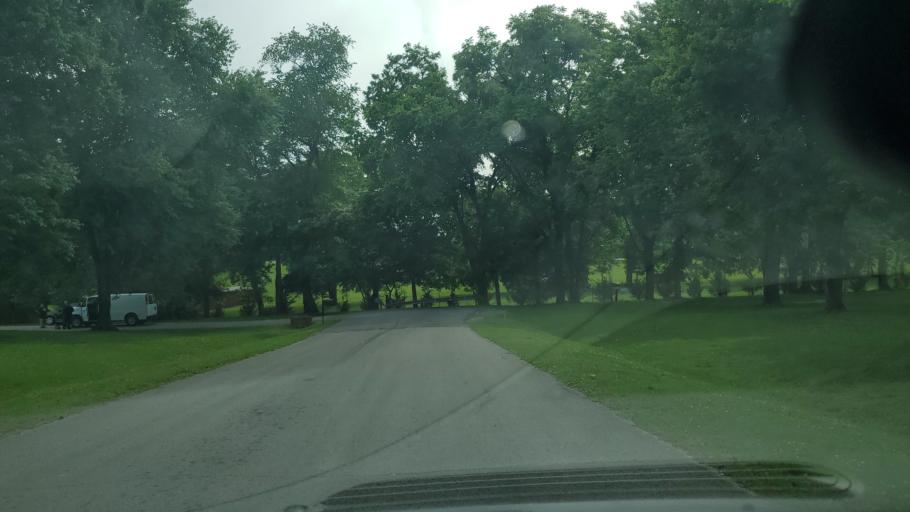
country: US
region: Tennessee
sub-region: Davidson County
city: Lakewood
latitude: 36.2208
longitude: -86.6864
